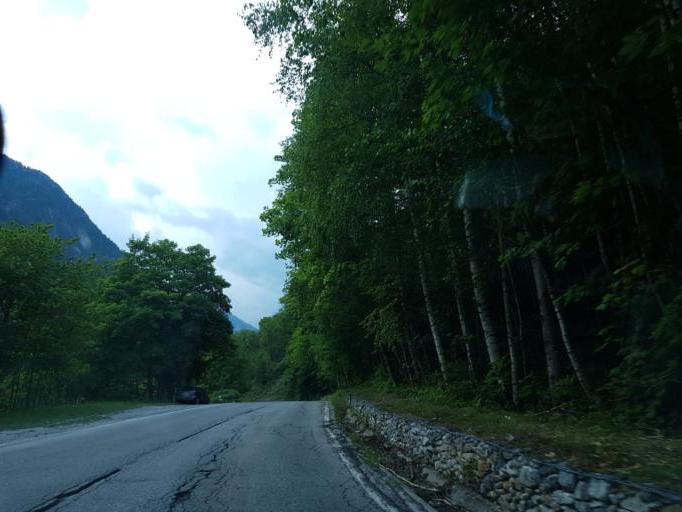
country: IT
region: Piedmont
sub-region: Provincia di Cuneo
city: Prazzo Superiore
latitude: 44.4773
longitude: 7.0455
